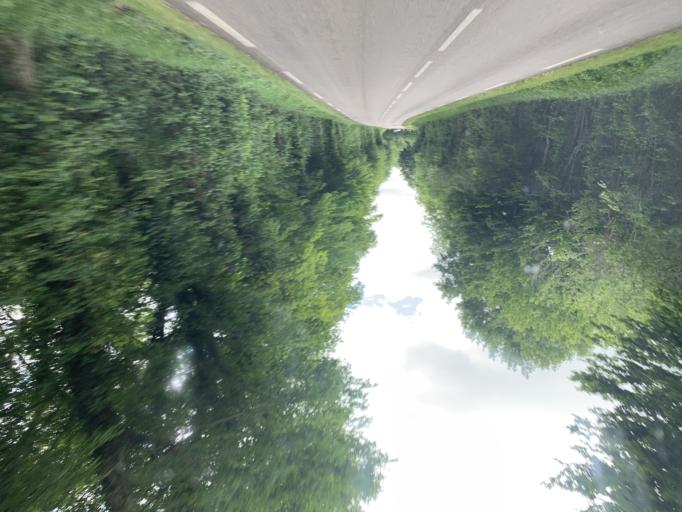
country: FR
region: Bourgogne
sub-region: Departement de l'Yonne
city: Chablis
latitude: 47.7375
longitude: 3.8111
